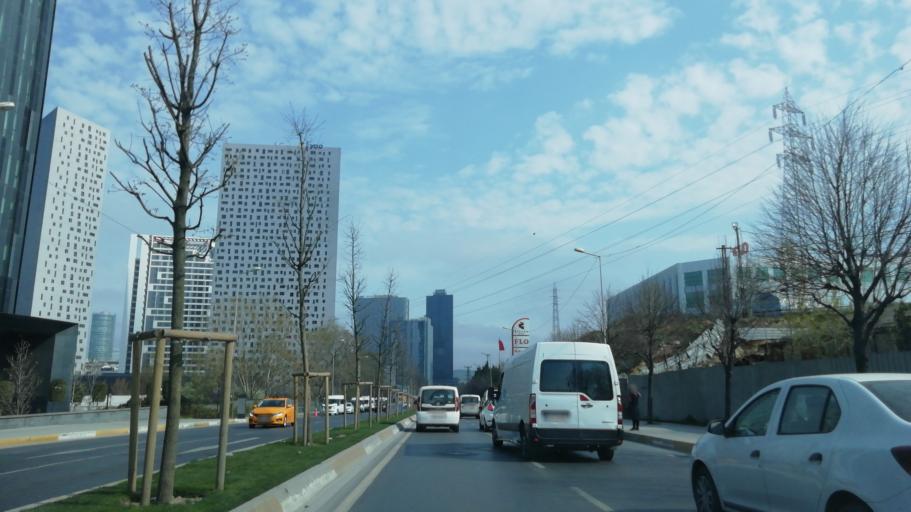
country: TR
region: Istanbul
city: Mahmutbey
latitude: 41.0520
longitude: 28.8127
